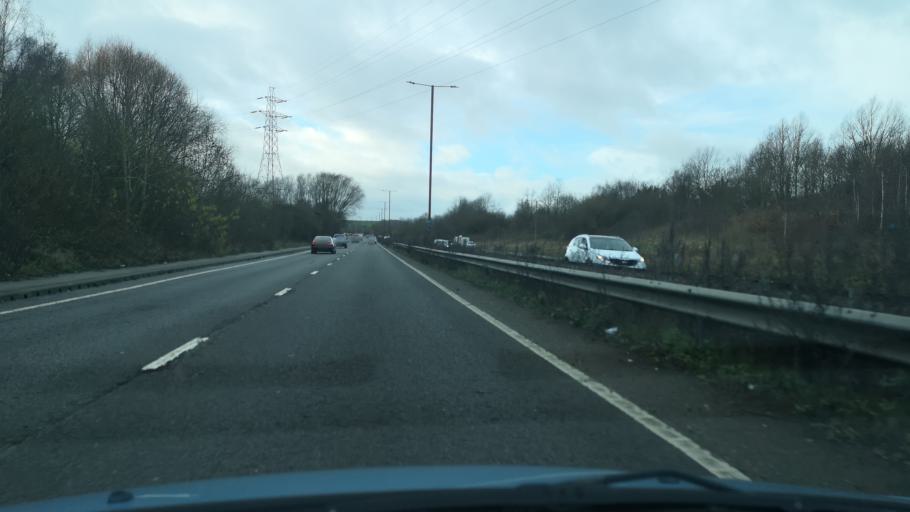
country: GB
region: England
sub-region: Barnsley
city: Wombwell
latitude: 53.5135
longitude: -1.3827
